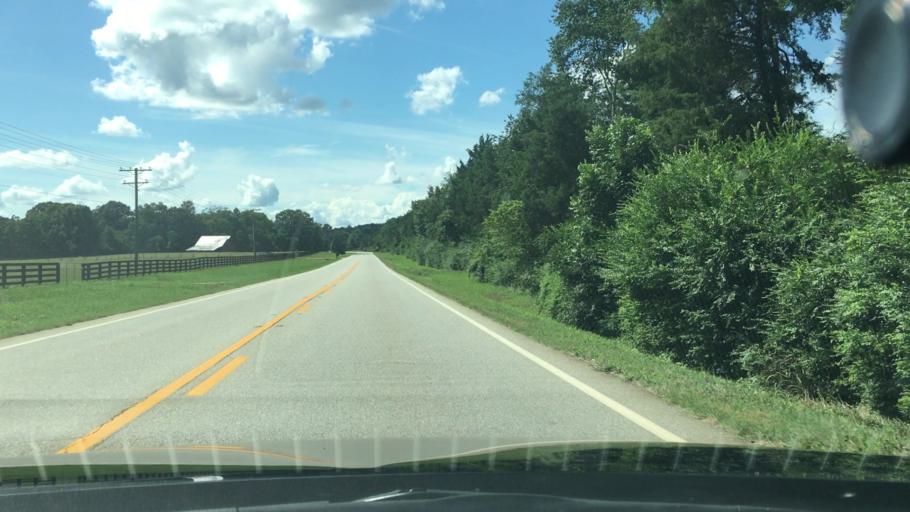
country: US
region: Georgia
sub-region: Jasper County
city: Monticello
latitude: 33.3129
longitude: -83.7475
